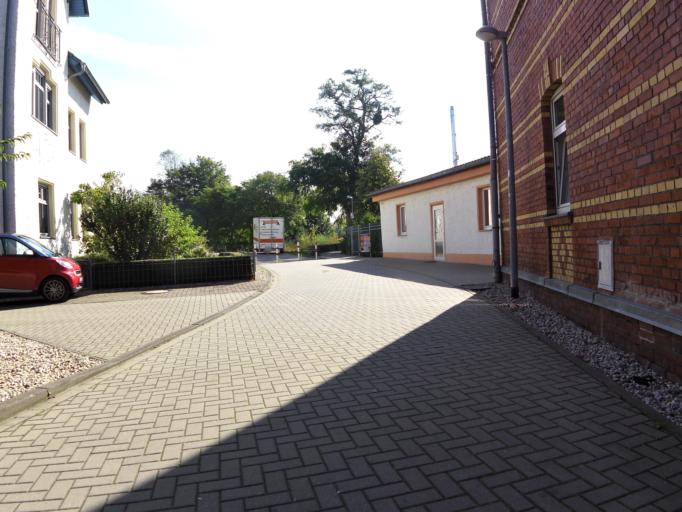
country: DE
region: Saxony-Anhalt
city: Wittenburg
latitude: 51.8637
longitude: 12.6148
